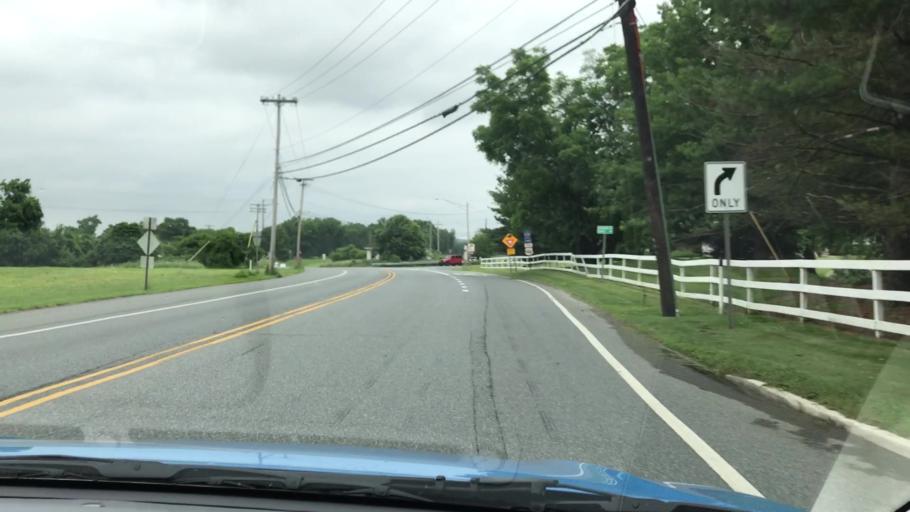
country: US
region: New Jersey
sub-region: Warren County
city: Belvidere
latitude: 40.8061
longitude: -75.0760
